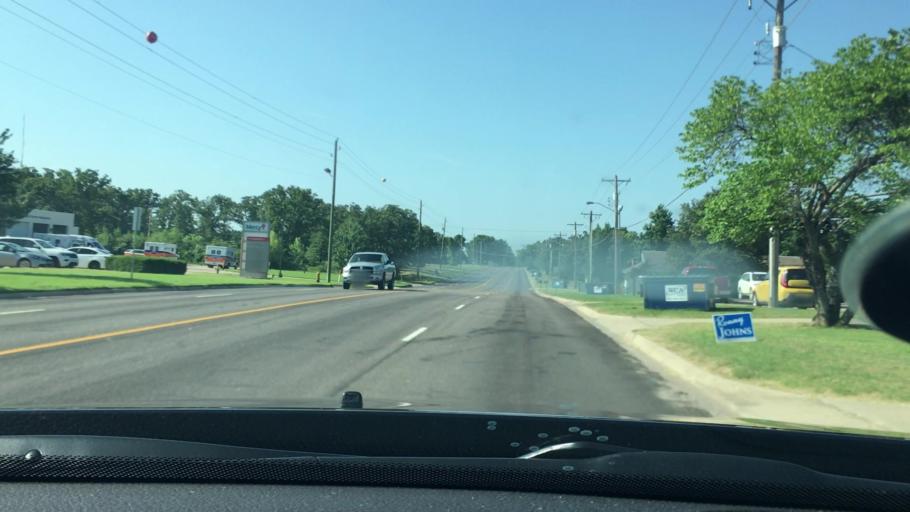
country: US
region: Oklahoma
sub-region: Pontotoc County
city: Ada
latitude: 34.7782
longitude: -96.6349
